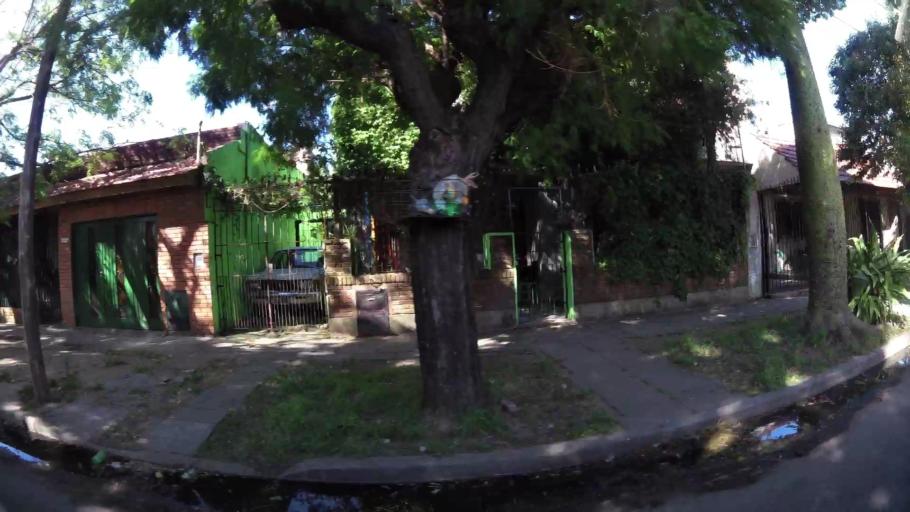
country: AR
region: Buenos Aires
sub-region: Partido de General San Martin
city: General San Martin
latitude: -34.5265
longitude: -58.5753
